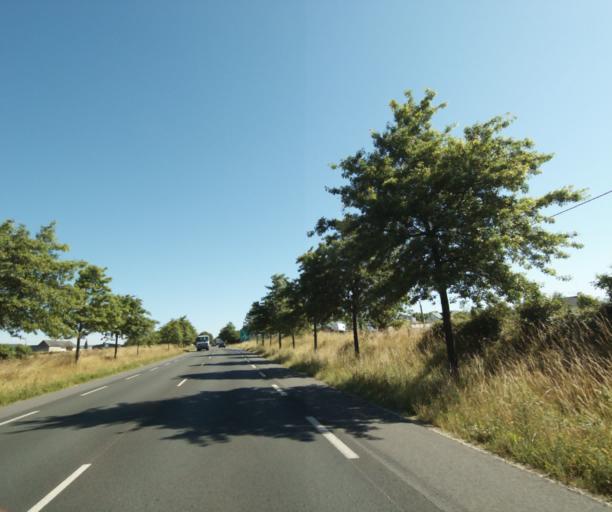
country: FR
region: Pays de la Loire
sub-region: Departement de la Mayenne
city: Bonchamp-les-Laval
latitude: 48.0684
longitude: -0.7314
